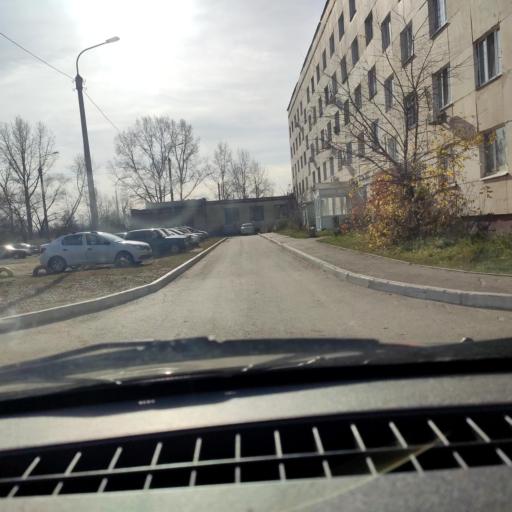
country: RU
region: Bashkortostan
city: Ufa
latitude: 54.6655
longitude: 55.9424
